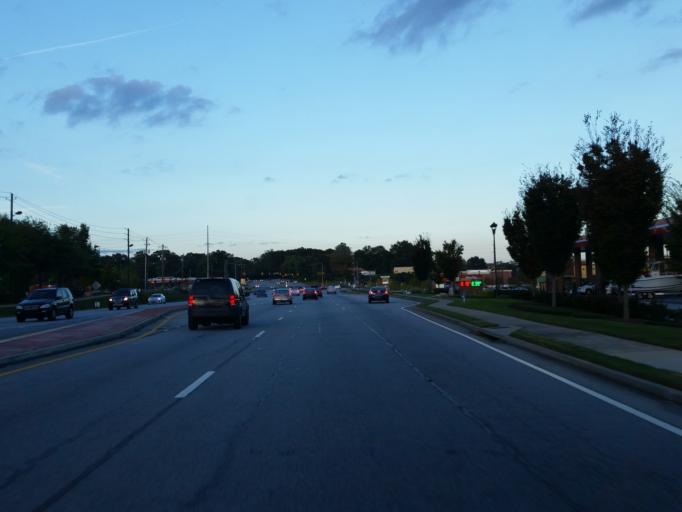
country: US
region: Georgia
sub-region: Cobb County
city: Smyrna
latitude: 33.8418
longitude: -84.5039
